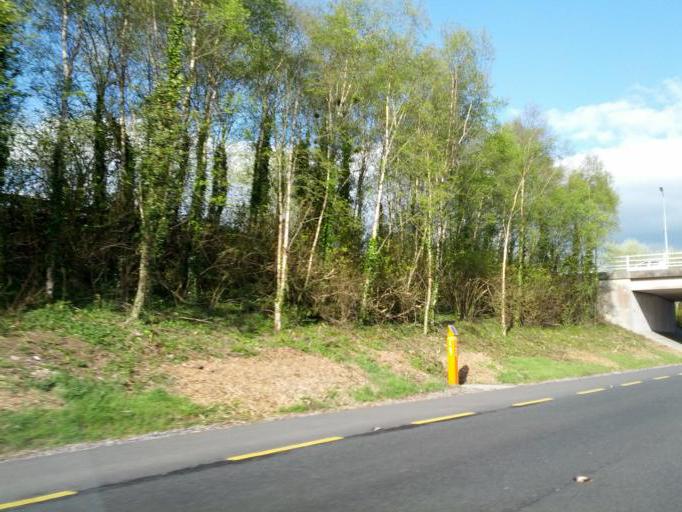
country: IE
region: Leinster
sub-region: An Iarmhi
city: Athlone
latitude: 53.4263
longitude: -7.9030
